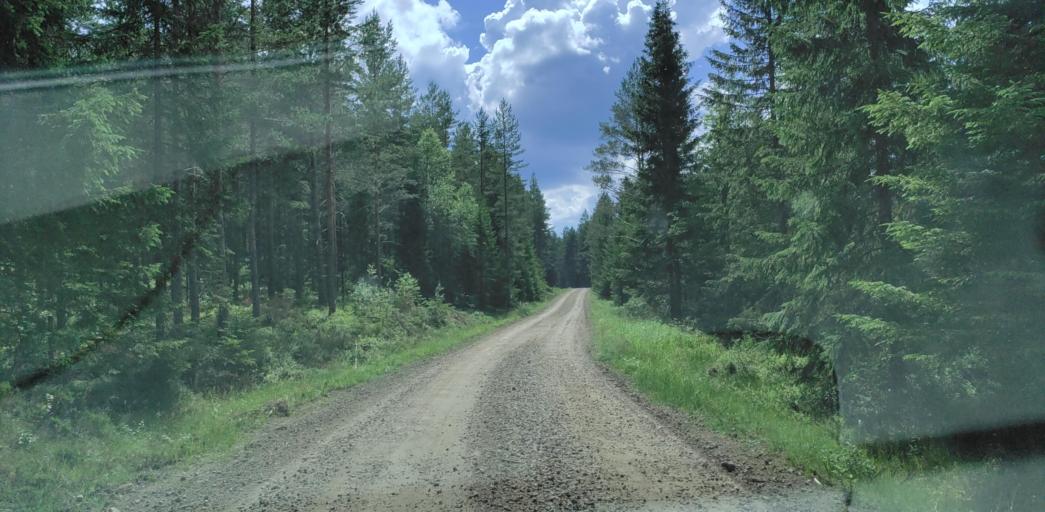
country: SE
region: Vaermland
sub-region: Hagfors Kommun
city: Ekshaerad
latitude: 60.0859
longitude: 13.3462
